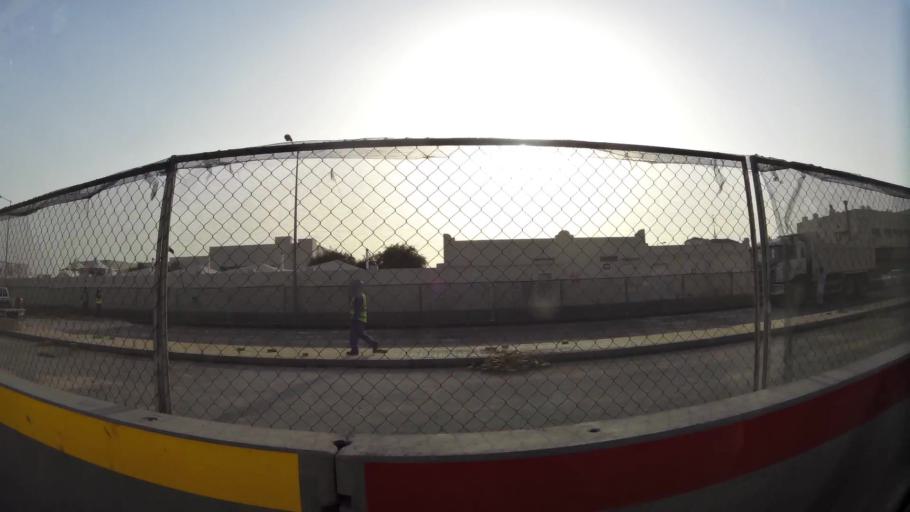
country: QA
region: Baladiyat ar Rayyan
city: Ar Rayyan
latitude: 25.2533
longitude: 51.4505
